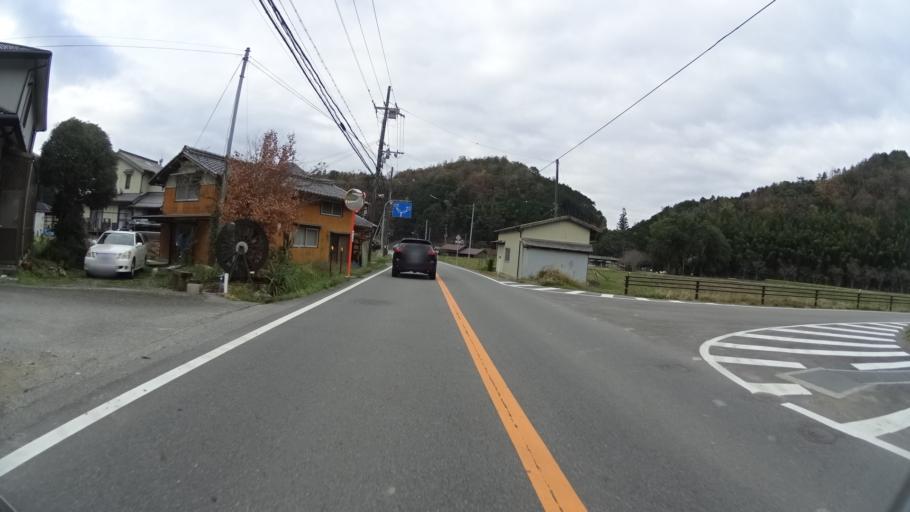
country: JP
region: Hyogo
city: Sasayama
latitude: 35.1344
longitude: 135.2226
